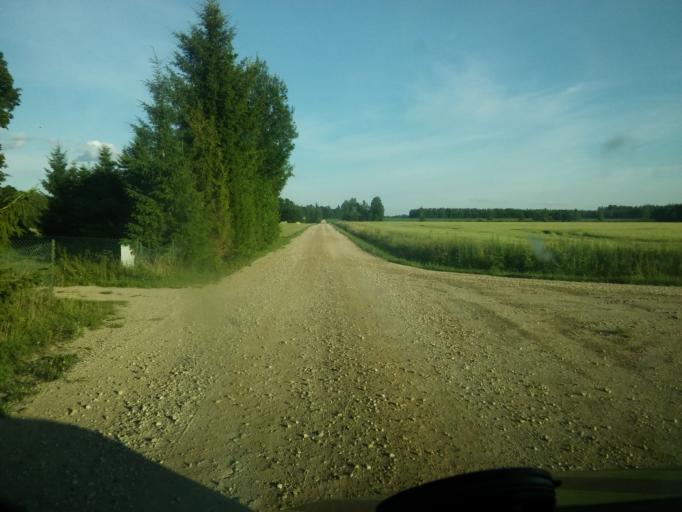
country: EE
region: Valgamaa
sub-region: Torva linn
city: Torva
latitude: 58.0654
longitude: 25.9077
